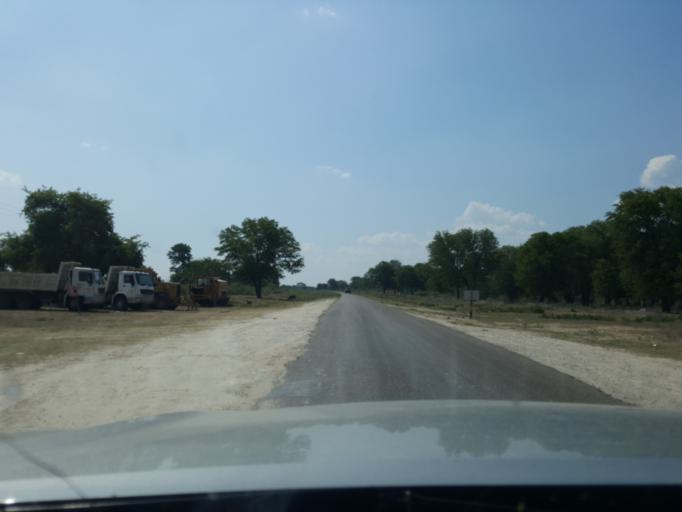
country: BW
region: North West
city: Shakawe
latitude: -18.8387
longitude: 22.2292
